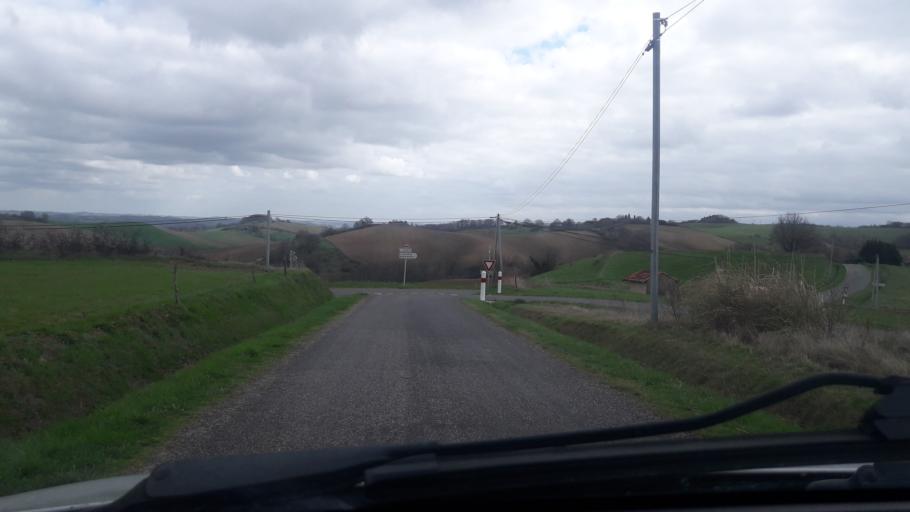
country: FR
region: Midi-Pyrenees
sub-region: Departement de l'Ariege
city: Lezat-sur-Leze
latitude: 43.2148
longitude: 1.3043
